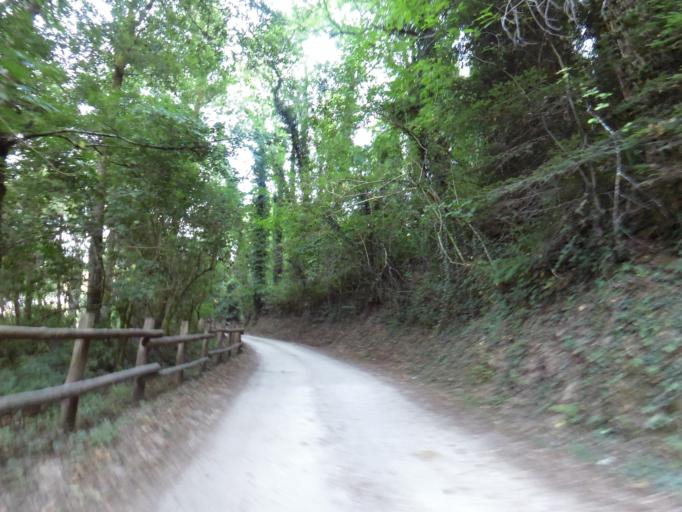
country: IT
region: Calabria
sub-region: Provincia di Vibo-Valentia
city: Mongiana
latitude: 38.5154
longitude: 16.3133
